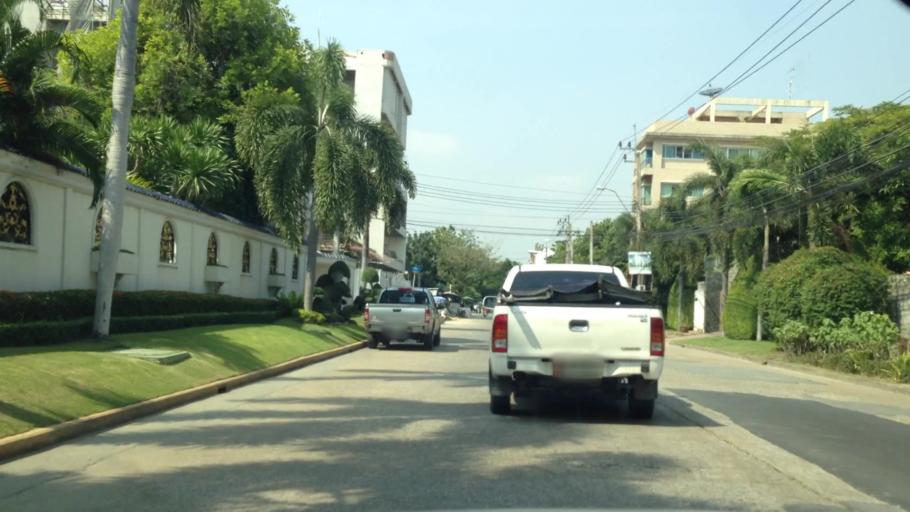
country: TH
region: Bangkok
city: Bang Na
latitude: 13.6857
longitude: 100.6512
